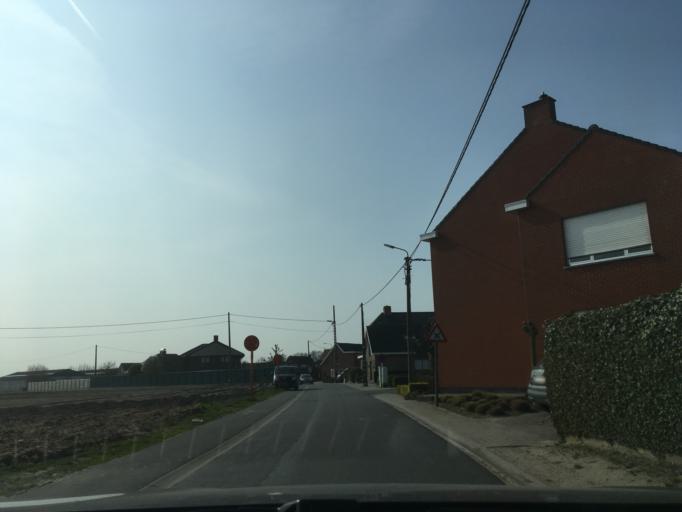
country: BE
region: Flanders
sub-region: Provincie West-Vlaanderen
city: Wingene
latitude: 51.0339
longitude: 3.2182
